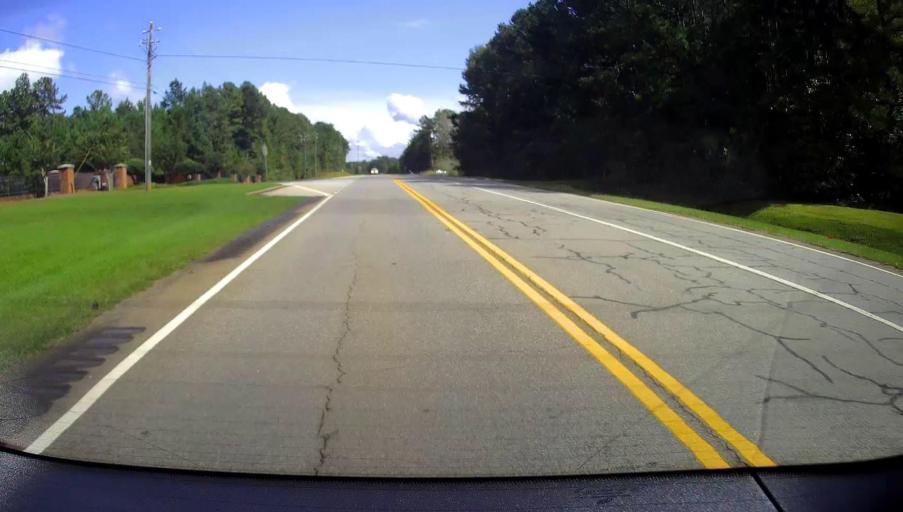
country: US
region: Georgia
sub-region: Jones County
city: Gray
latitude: 33.0280
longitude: -83.4551
